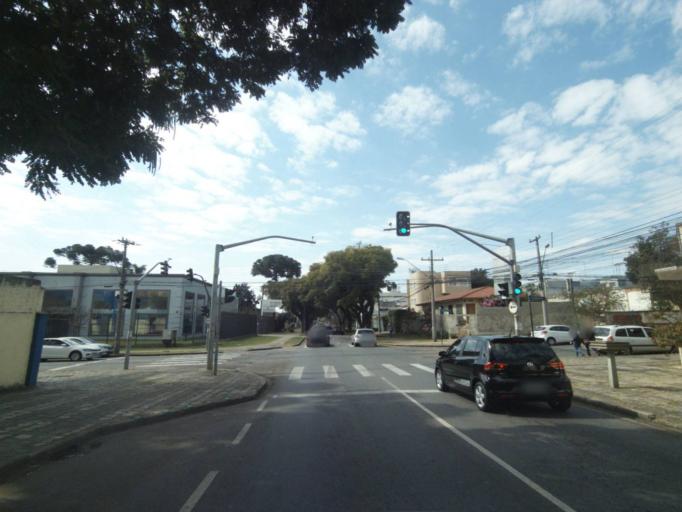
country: BR
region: Parana
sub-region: Curitiba
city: Curitiba
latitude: -25.4535
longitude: -49.2693
